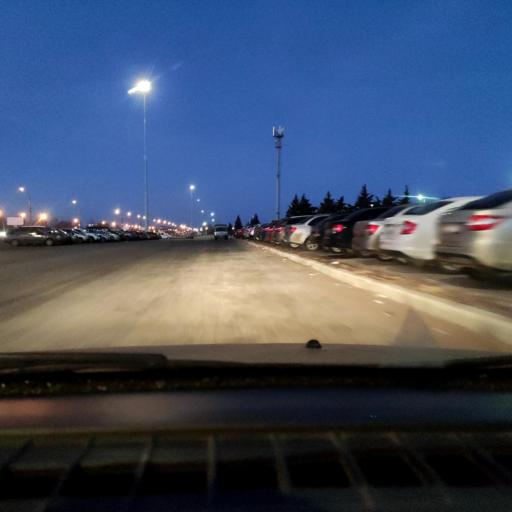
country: RU
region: Samara
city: Tol'yatti
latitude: 53.5573
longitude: 49.2473
